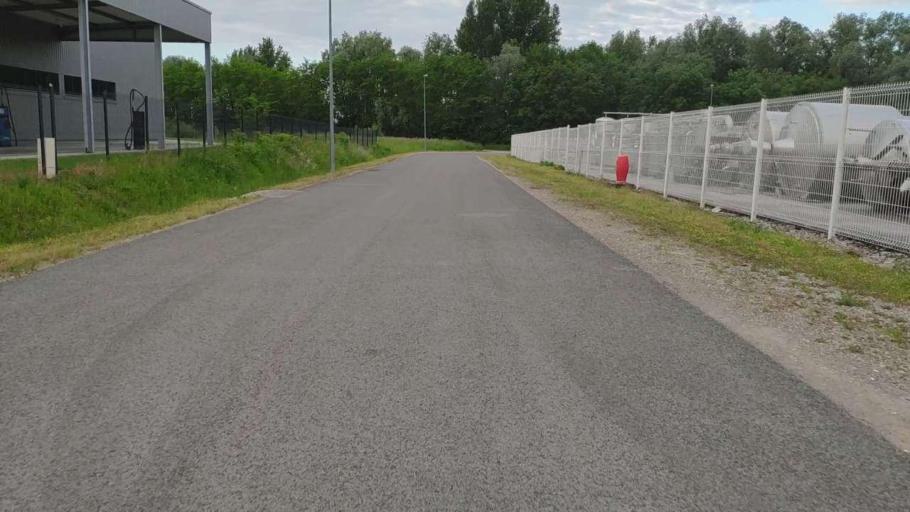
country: FR
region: Franche-Comte
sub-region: Departement du Jura
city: Bletterans
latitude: 46.7479
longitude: 5.4729
